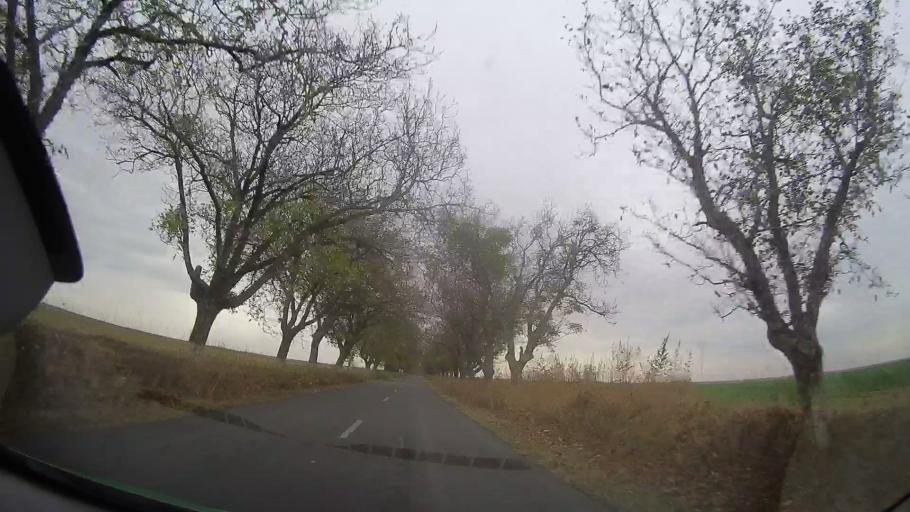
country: RO
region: Prahova
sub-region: Comuna Fantanele
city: Fantanele
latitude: 45.0185
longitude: 26.3975
